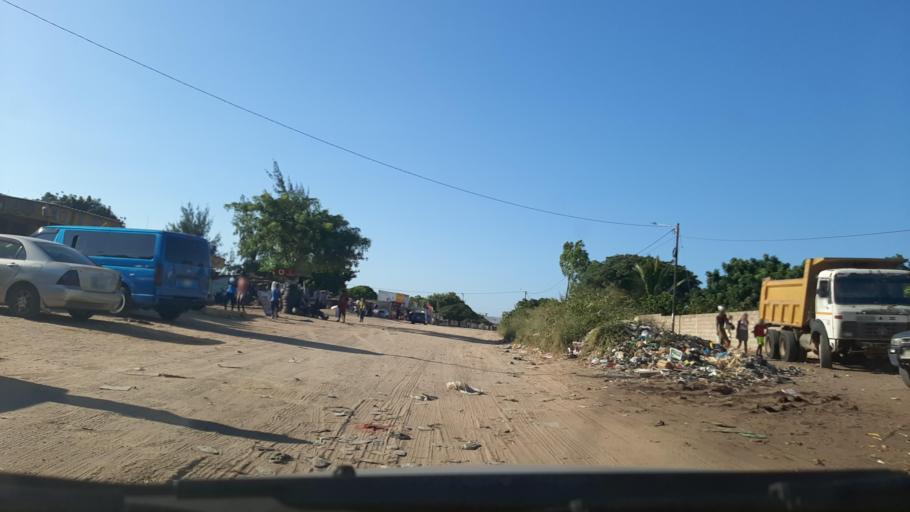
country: MZ
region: Maputo City
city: Maputo
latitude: -25.8096
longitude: 32.5462
